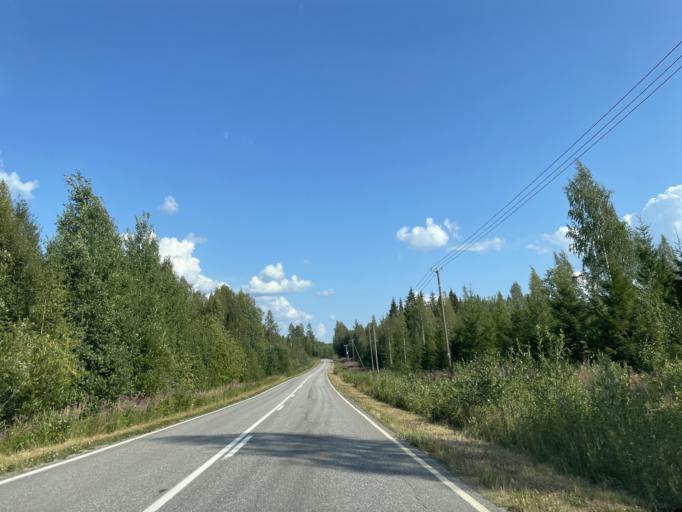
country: FI
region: Central Finland
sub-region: Saarijaervi-Viitasaari
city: Pihtipudas
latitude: 63.3538
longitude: 25.7740
